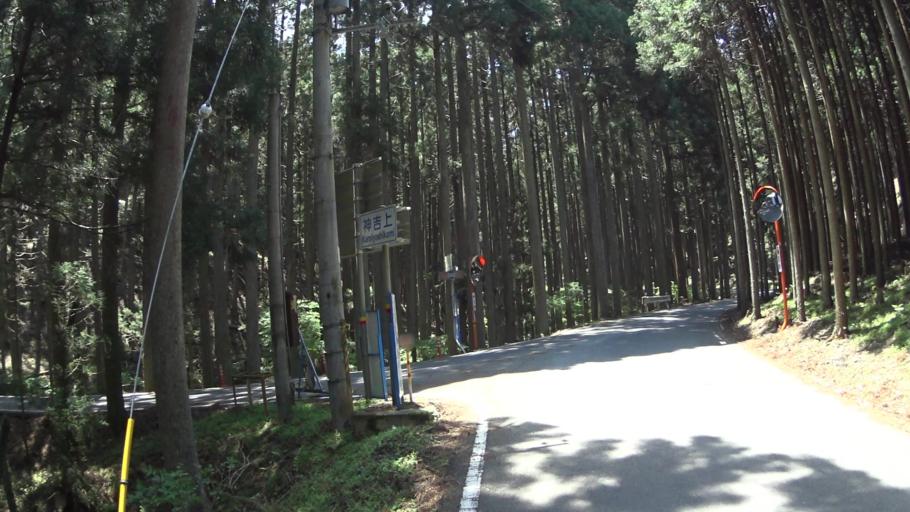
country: JP
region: Kyoto
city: Kameoka
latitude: 35.1146
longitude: 135.5848
